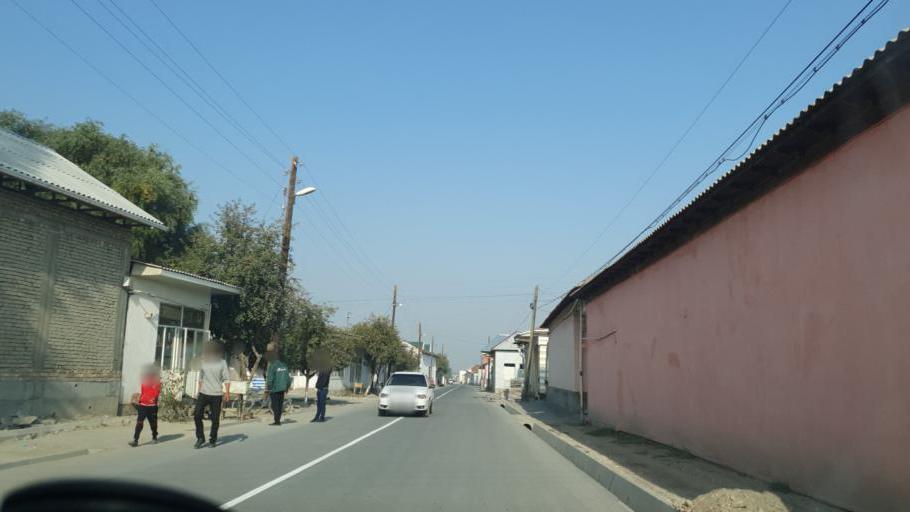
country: UZ
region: Fergana
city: Qo`qon
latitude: 40.5841
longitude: 70.9083
